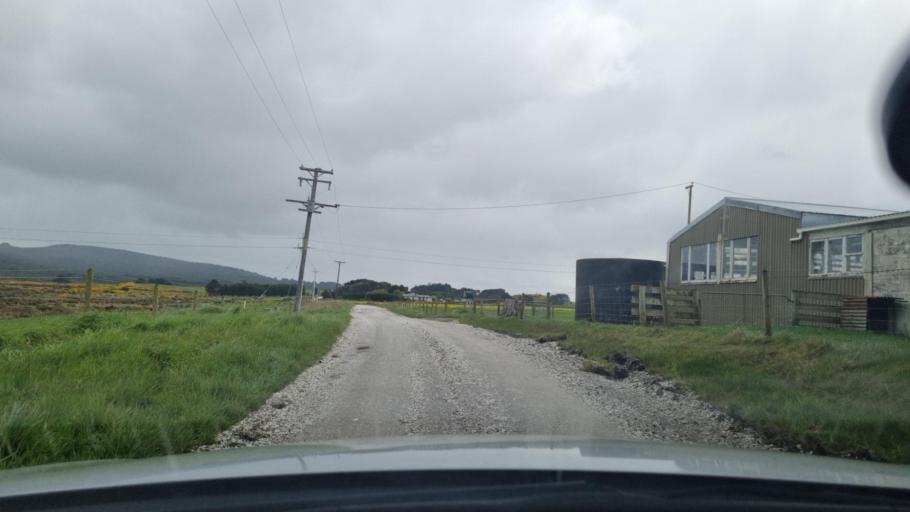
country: NZ
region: Southland
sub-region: Invercargill City
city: Bluff
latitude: -46.5453
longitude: 168.2984
